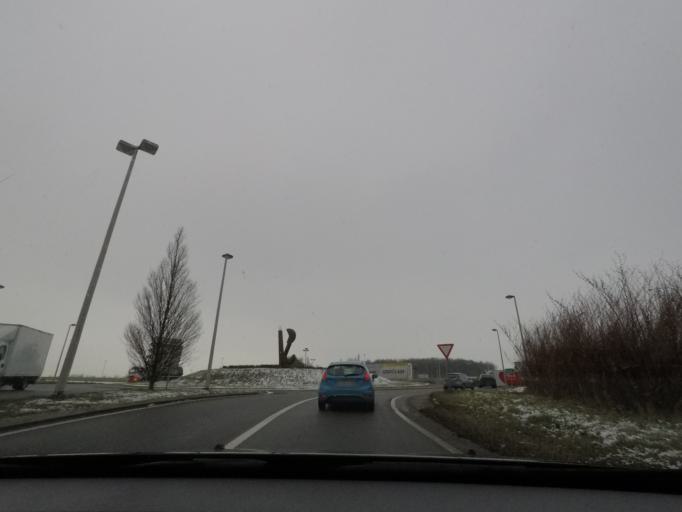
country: BE
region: Wallonia
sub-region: Province de Namur
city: Sombreffe
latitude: 50.4845
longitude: 4.6035
